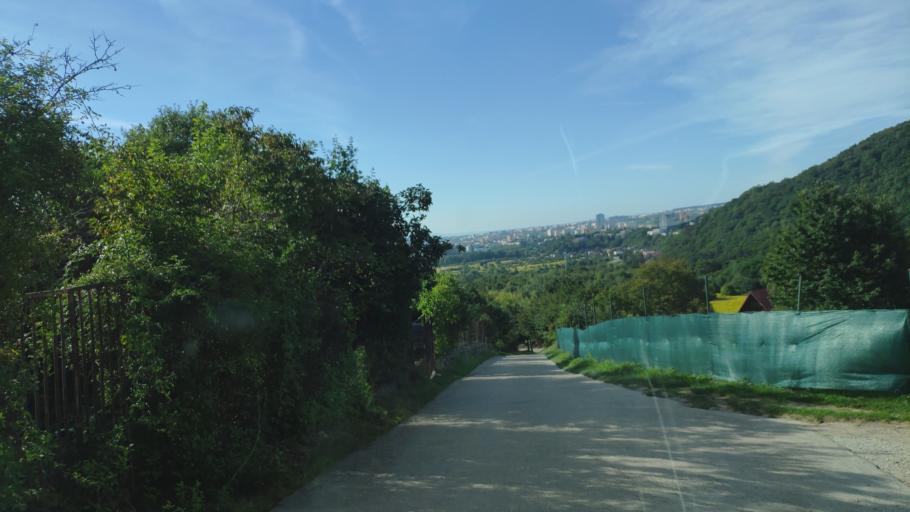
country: SK
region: Kosicky
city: Kosice
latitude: 48.7649
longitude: 21.2509
